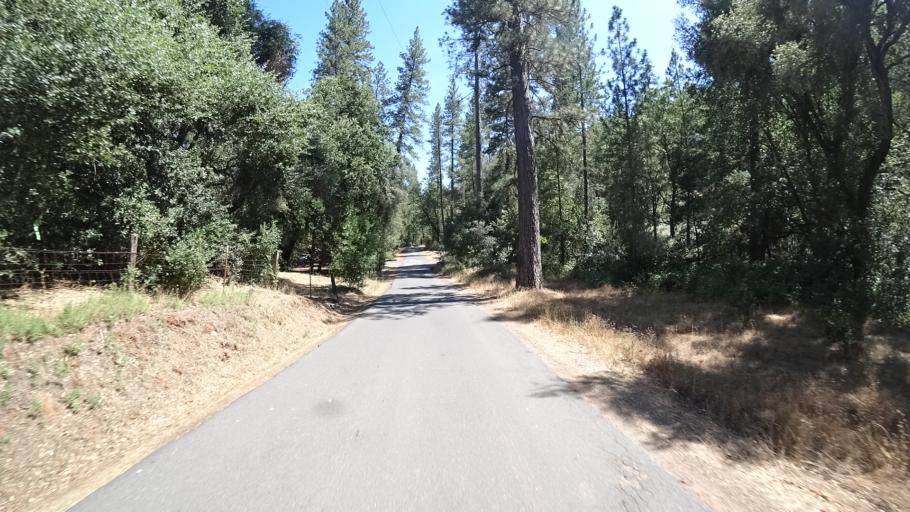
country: US
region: California
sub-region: Calaveras County
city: Murphys
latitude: 38.1573
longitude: -120.4739
